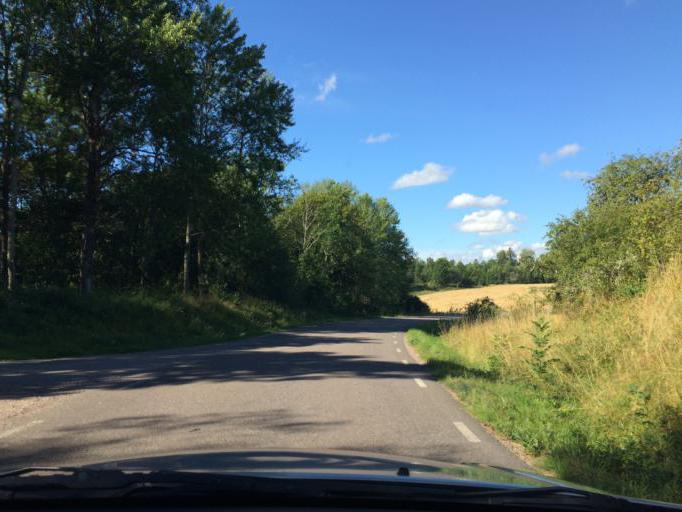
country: SE
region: Soedermanland
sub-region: Eskilstuna Kommun
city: Torshalla
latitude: 59.5072
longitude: 16.4122
